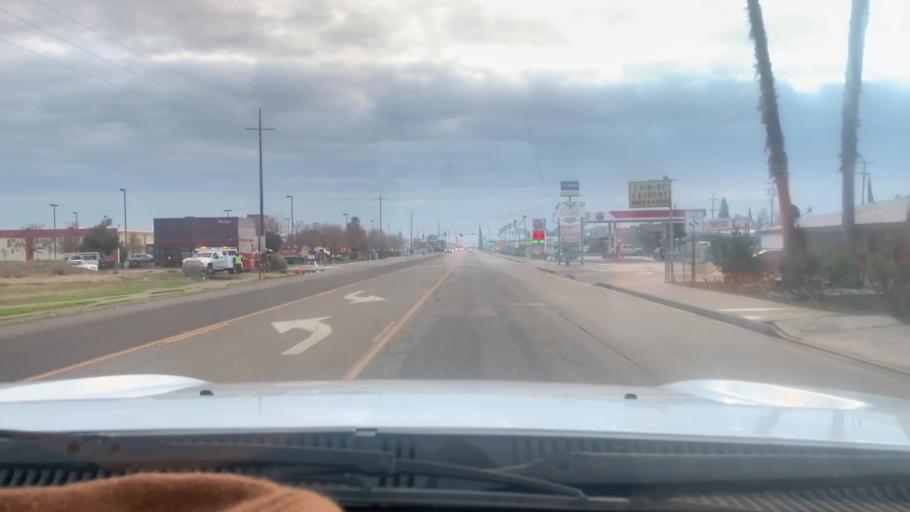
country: US
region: California
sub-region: Kern County
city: Wasco
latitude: 35.6015
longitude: -119.3436
